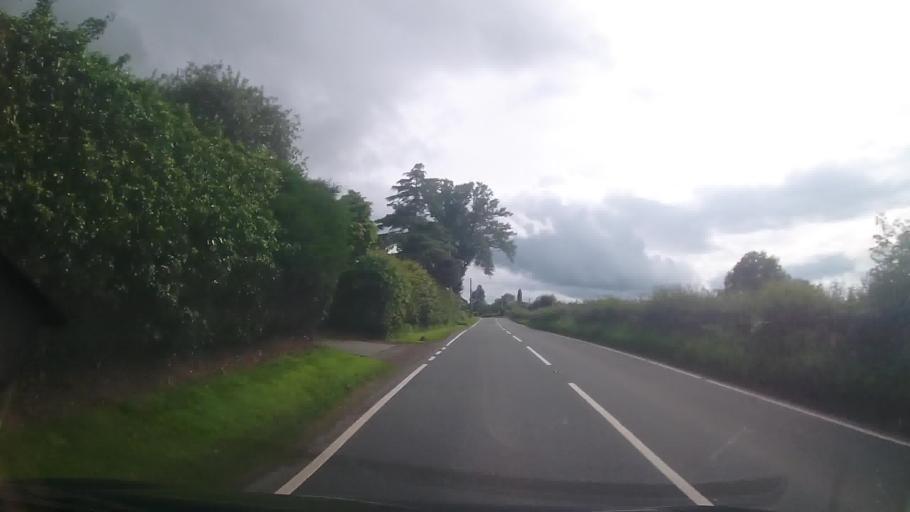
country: GB
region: England
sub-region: Shropshire
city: Whitchurch
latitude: 52.9606
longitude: -2.7342
